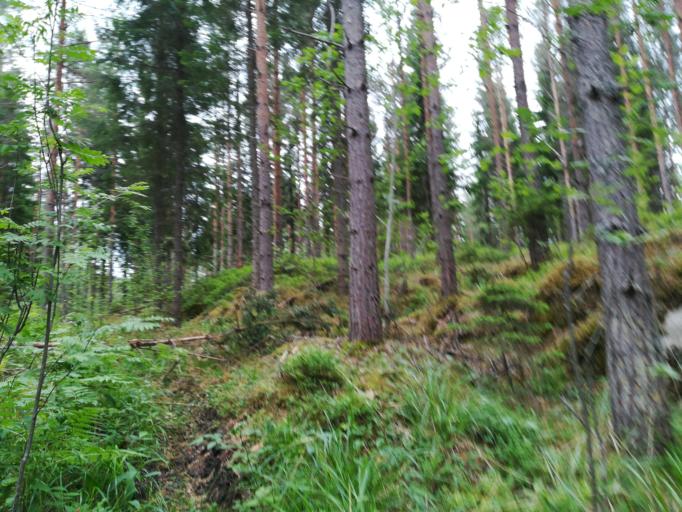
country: FI
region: South Karelia
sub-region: Lappeenranta
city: Savitaipale
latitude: 61.3032
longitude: 27.6179
